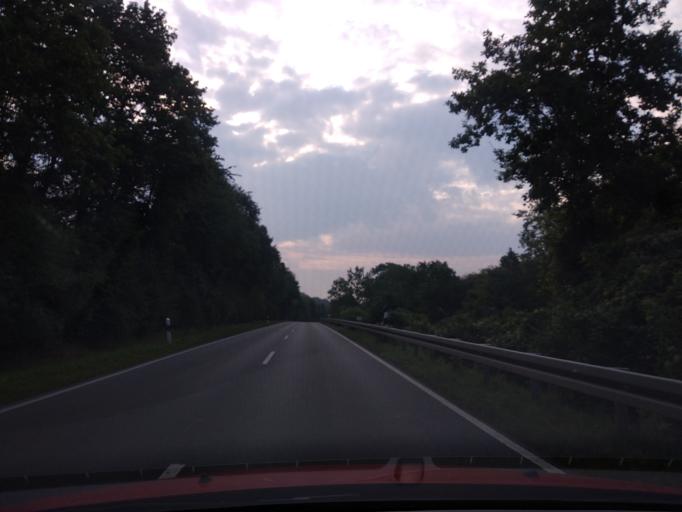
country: DE
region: Hesse
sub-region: Regierungsbezirk Kassel
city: Calden
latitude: 51.3785
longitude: 9.3736
